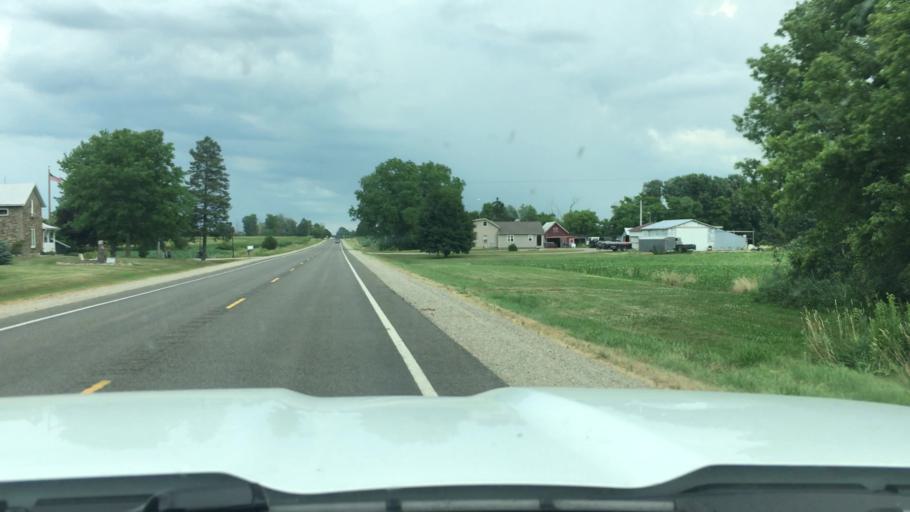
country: US
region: Michigan
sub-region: Montcalm County
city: Carson City
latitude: 43.1775
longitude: -84.9283
